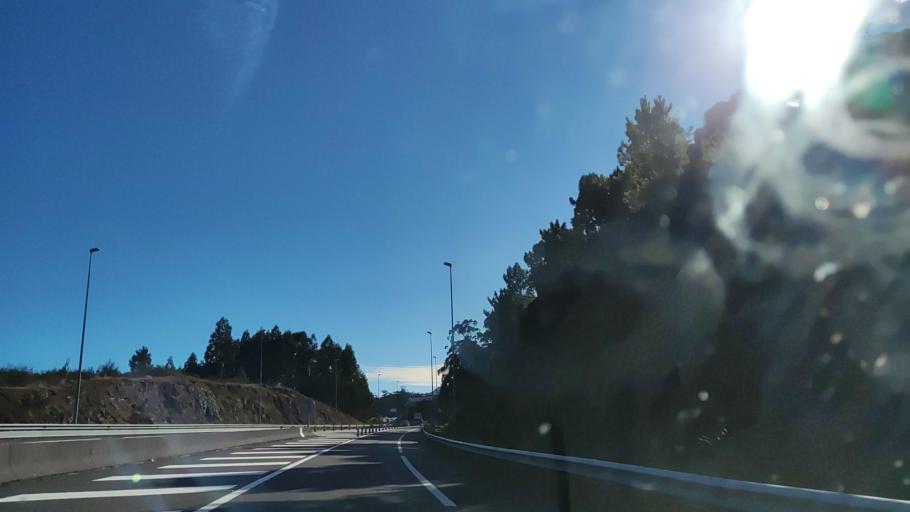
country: ES
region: Galicia
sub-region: Provincia da Coruna
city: Boiro
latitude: 42.5755
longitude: -8.9927
